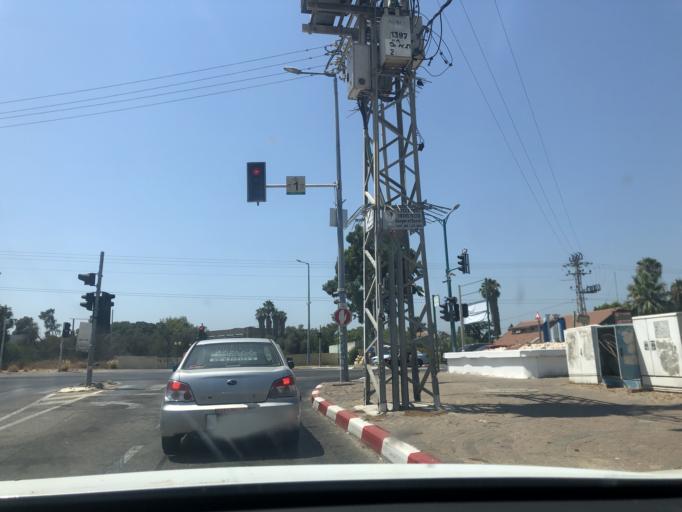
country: IL
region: Central District
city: Lod
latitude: 31.9381
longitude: 34.8863
